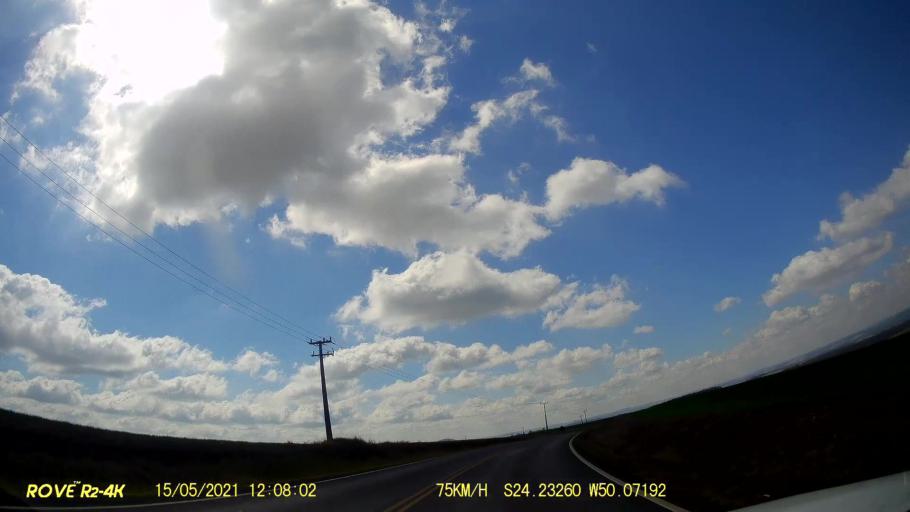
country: BR
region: Parana
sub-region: Pirai Do Sul
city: Pirai do Sul
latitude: -24.2326
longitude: -50.0719
